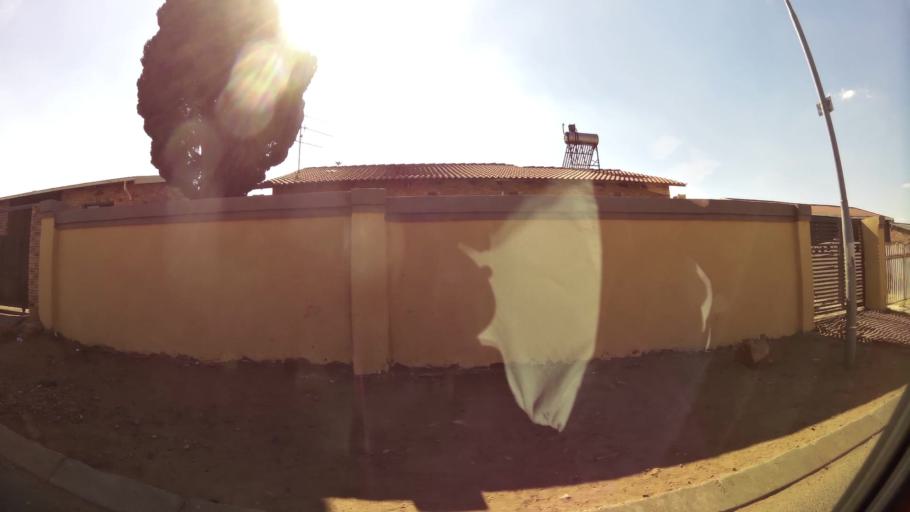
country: ZA
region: Gauteng
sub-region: City of Johannesburg Metropolitan Municipality
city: Soweto
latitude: -26.2417
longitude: 27.9049
